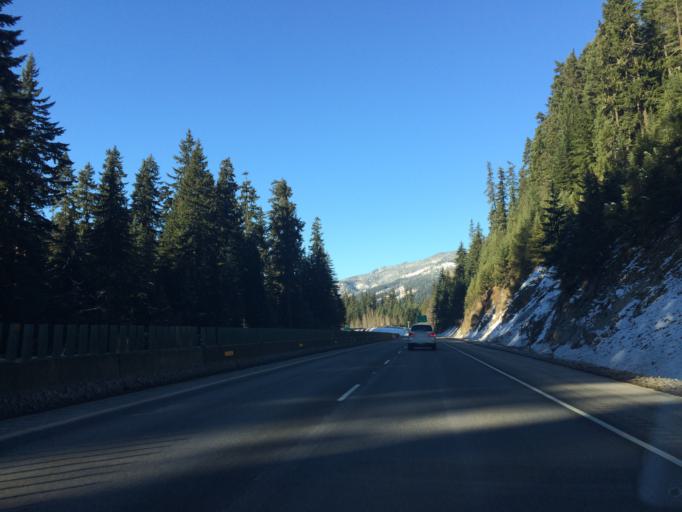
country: US
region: Washington
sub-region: Kittitas County
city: Cle Elum
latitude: 47.2926
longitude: -121.2845
